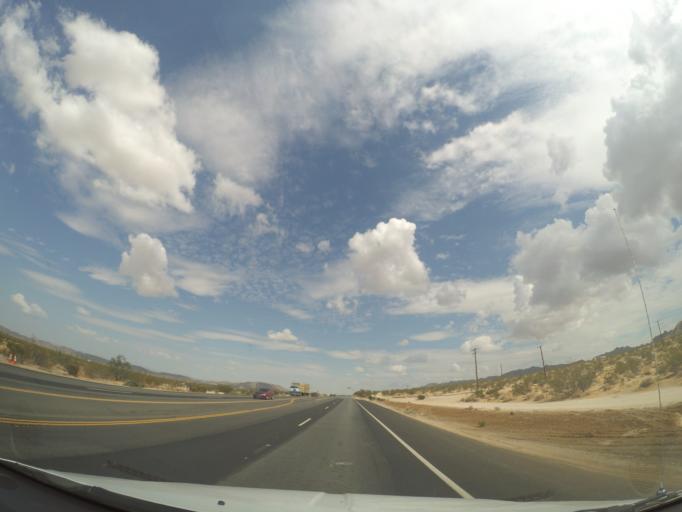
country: US
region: California
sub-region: San Bernardino County
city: Joshua Tree
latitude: 34.1350
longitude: -116.2837
